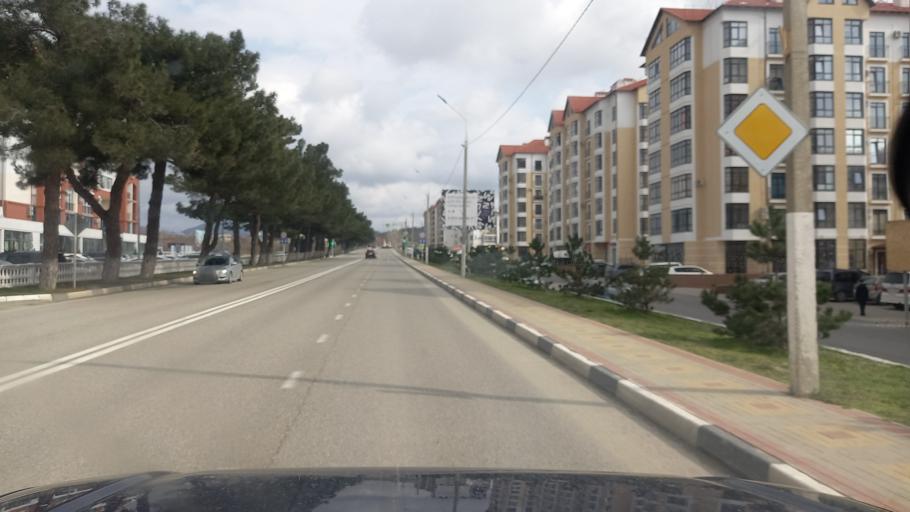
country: RU
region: Krasnodarskiy
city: Gelendzhik
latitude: 44.5568
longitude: 38.1044
